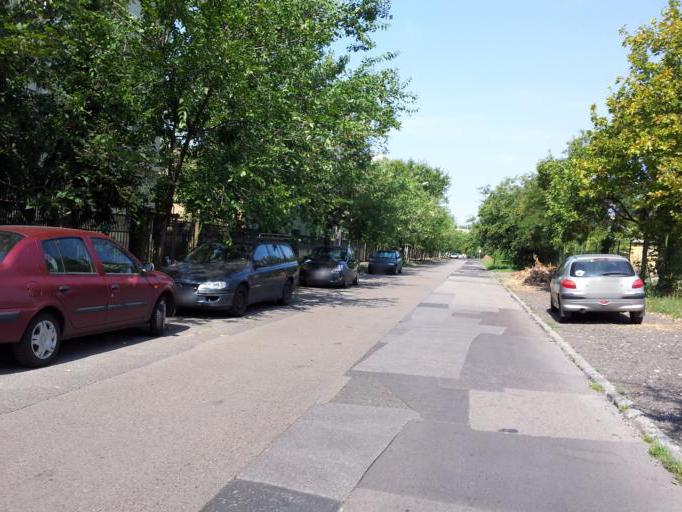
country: HU
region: Budapest
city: Budapest XIV. keruelet
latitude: 47.5090
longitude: 19.1150
